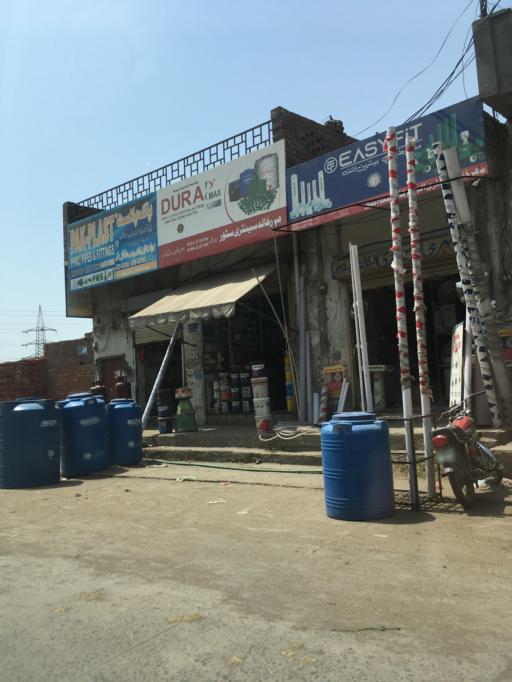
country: PK
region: Punjab
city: Lahore
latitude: 31.6113
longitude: 74.3389
